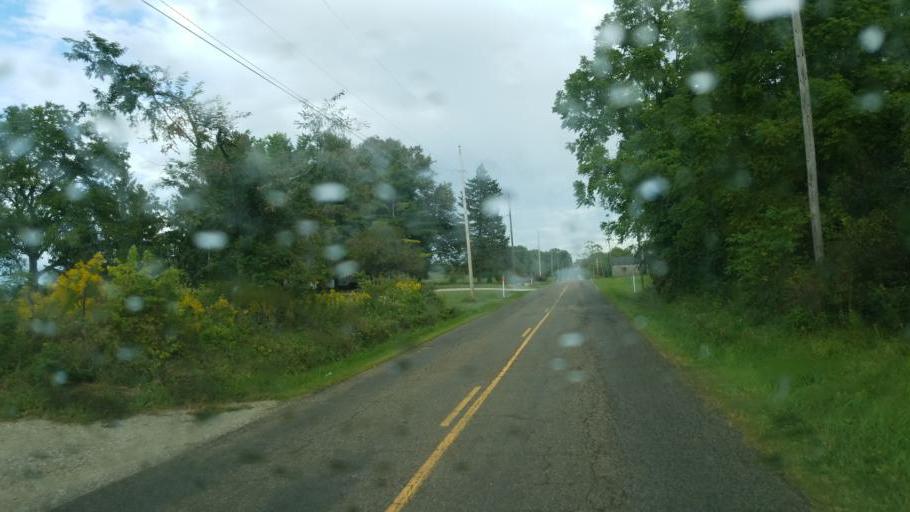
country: US
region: Ohio
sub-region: Knox County
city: Centerburg
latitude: 40.3220
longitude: -82.7345
